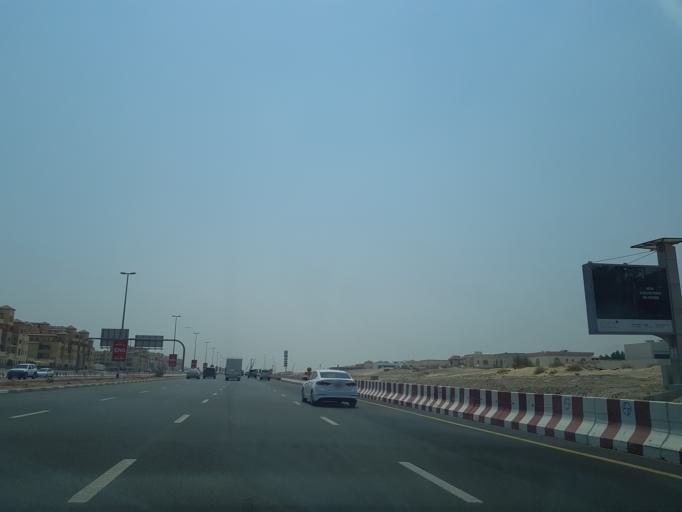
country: AE
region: Ash Shariqah
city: Sharjah
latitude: 25.2110
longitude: 55.4126
